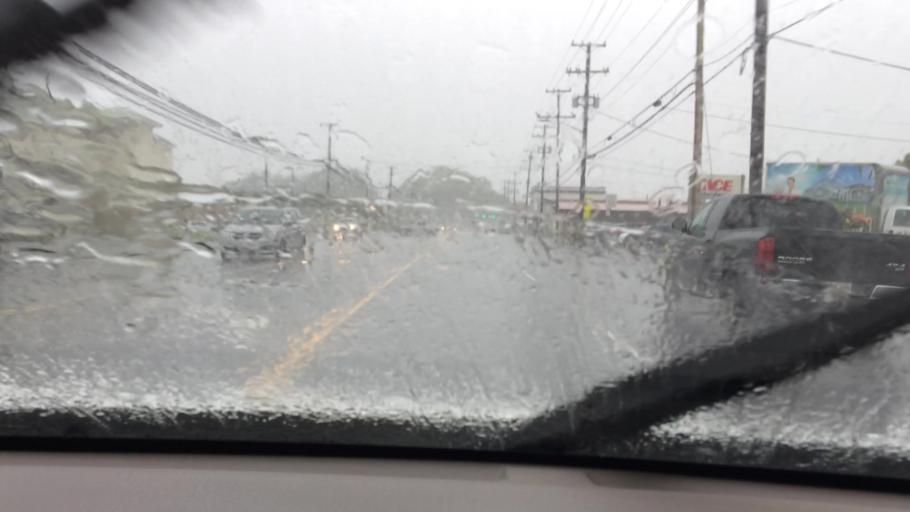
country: US
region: Hawaii
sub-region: Hawaii County
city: Hilo
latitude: 19.7180
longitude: -155.0805
